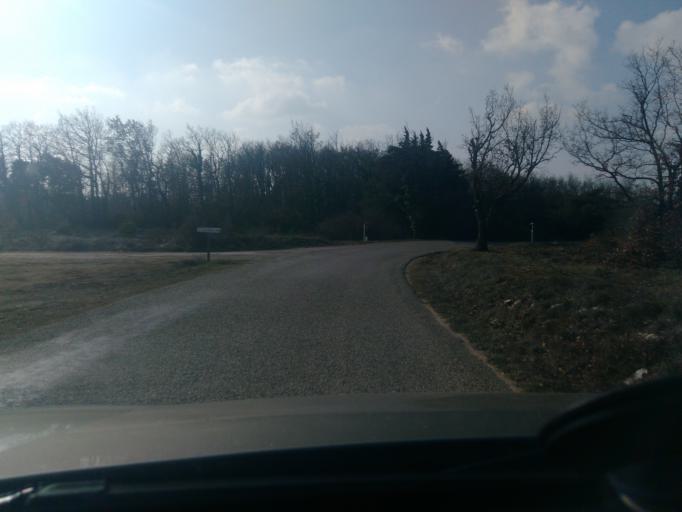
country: FR
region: Rhone-Alpes
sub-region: Departement de la Drome
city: Grignan
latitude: 44.4784
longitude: 4.8626
